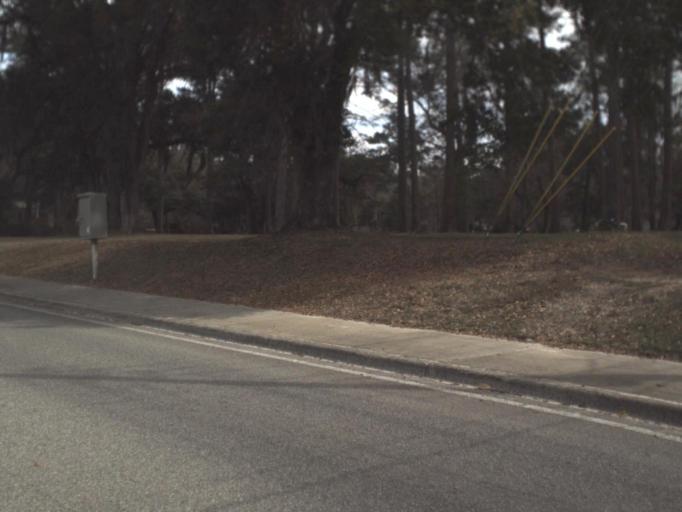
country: US
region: Florida
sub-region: Leon County
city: Tallahassee
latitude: 30.5116
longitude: -84.2454
